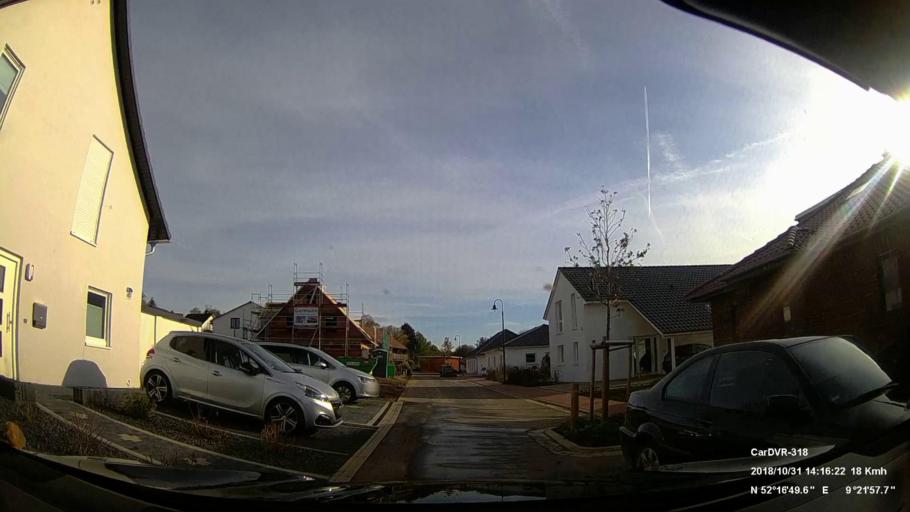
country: DE
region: Lower Saxony
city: Lauenau
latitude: 52.2804
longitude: 9.3661
